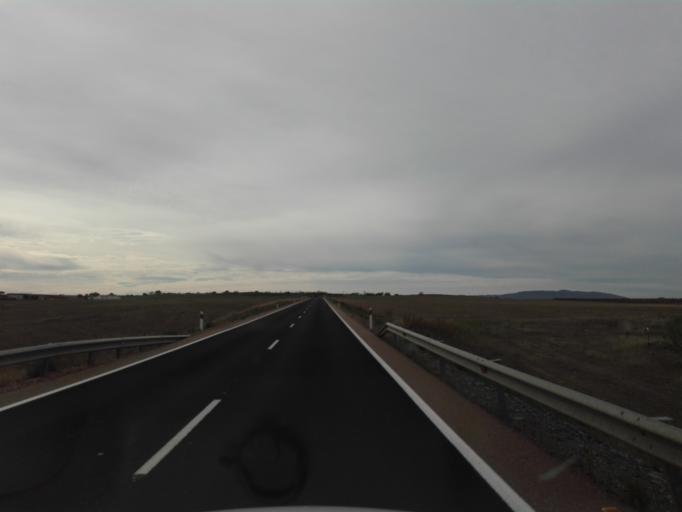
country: ES
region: Extremadura
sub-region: Provincia de Badajoz
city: Valencia de las Torres
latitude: 38.3299
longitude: -5.9641
